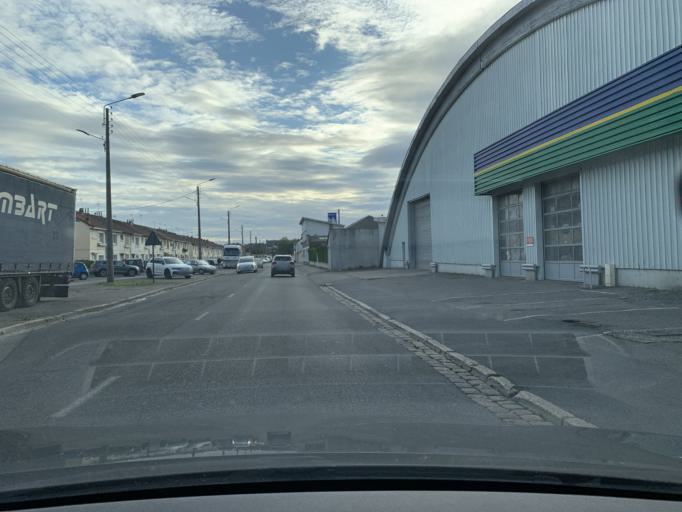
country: FR
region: Picardie
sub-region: Departement de l'Aisne
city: Harly
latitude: 49.8455
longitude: 3.3004
